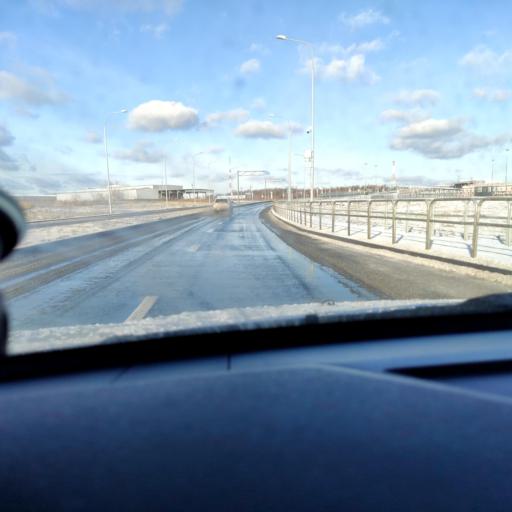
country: RU
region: Samara
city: Samara
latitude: 53.2739
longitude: 50.2320
